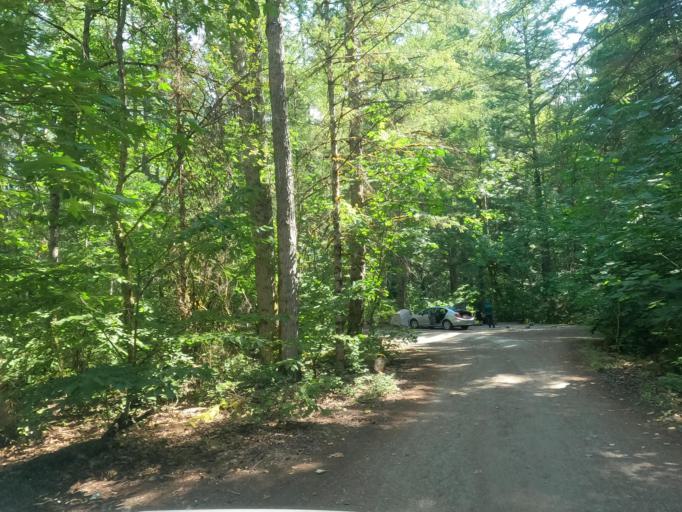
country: CA
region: British Columbia
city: Pemberton
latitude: 50.3502
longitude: -122.7301
